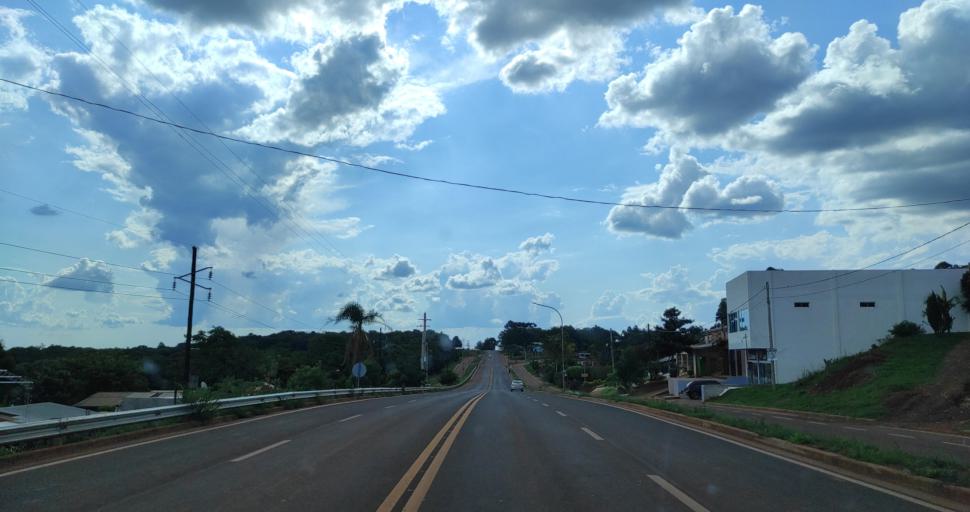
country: AR
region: Misiones
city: Bernardo de Irigoyen
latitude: -26.2937
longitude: -53.7612
